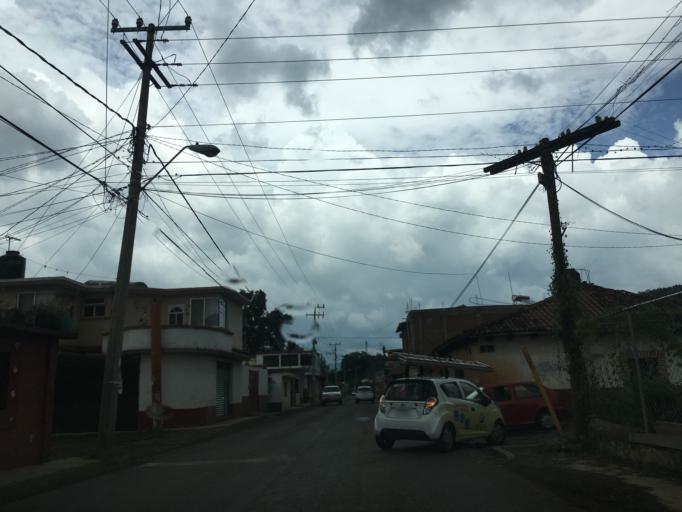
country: MX
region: Michoacan
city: Patzcuaro
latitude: 19.5337
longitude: -101.6176
